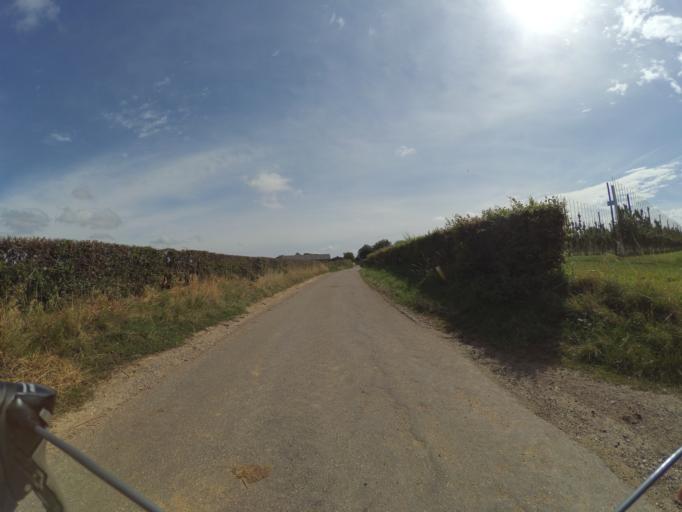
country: NL
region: Limburg
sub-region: Eijsden-Margraten
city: Margraten
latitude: 50.8066
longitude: 5.7989
